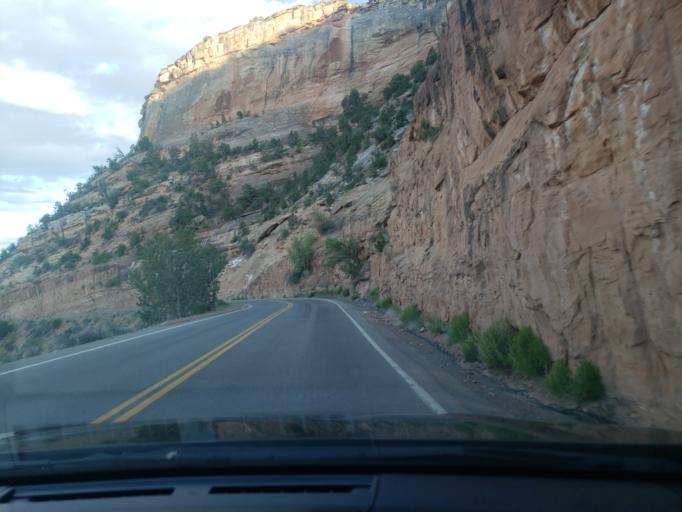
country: US
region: Colorado
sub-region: Mesa County
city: Fruita
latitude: 39.1155
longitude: -108.7276
